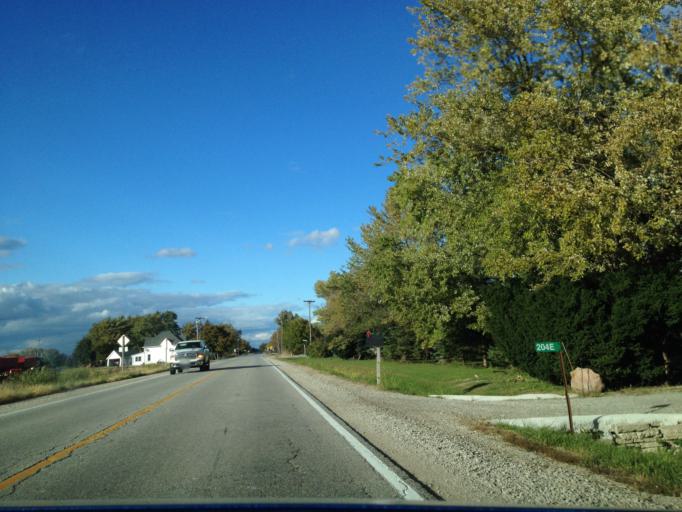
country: US
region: Michigan
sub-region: Wayne County
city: Grosse Pointe
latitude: 42.1367
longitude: -82.7336
